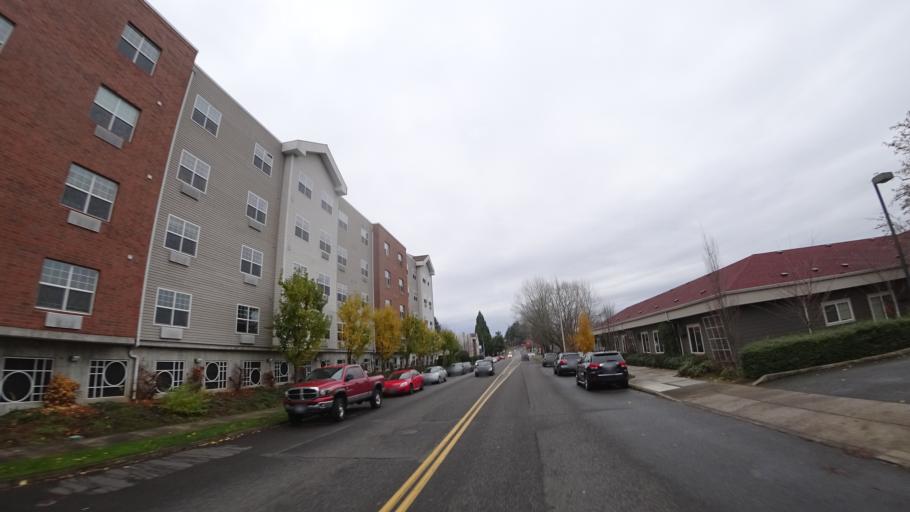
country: US
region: Oregon
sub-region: Multnomah County
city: Lents
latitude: 45.5143
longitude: -122.5526
